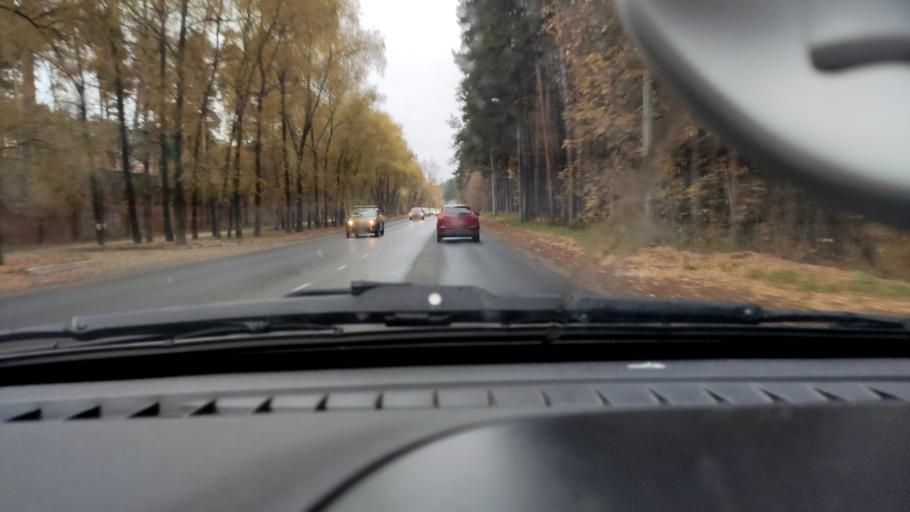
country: RU
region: Perm
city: Kultayevo
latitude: 58.0095
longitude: 55.9776
